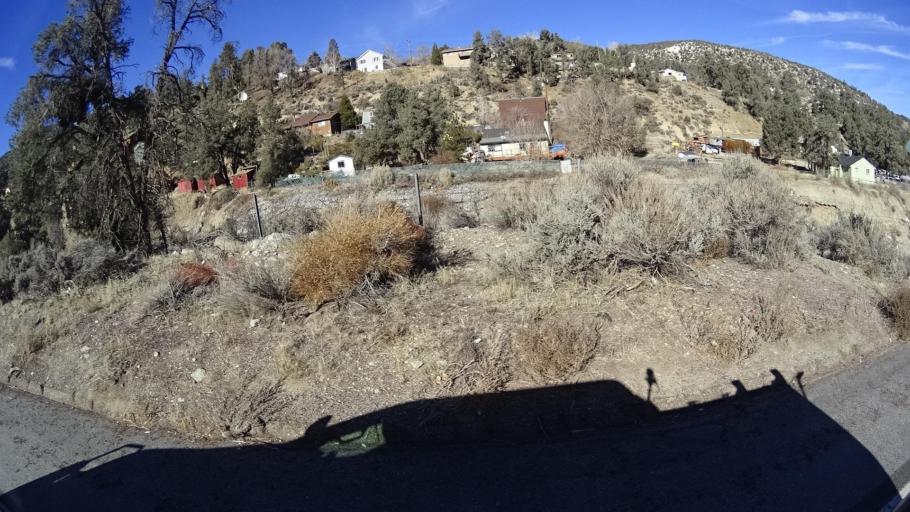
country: US
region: California
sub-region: Kern County
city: Frazier Park
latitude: 34.8201
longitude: -118.9552
